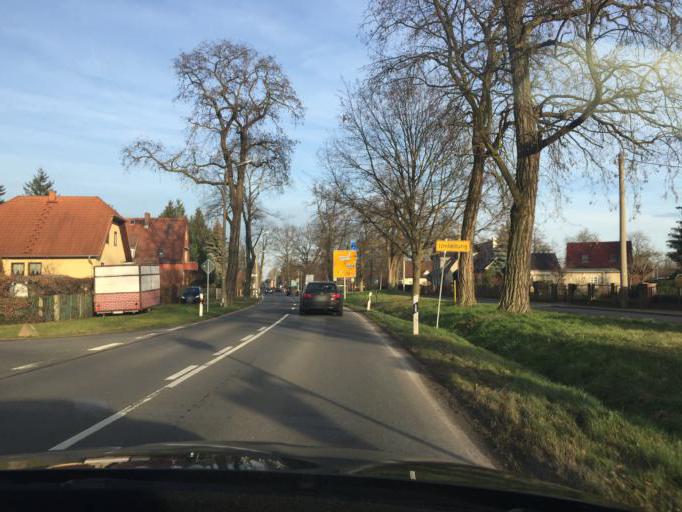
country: DE
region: Brandenburg
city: Forst
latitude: 51.7292
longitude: 14.6256
